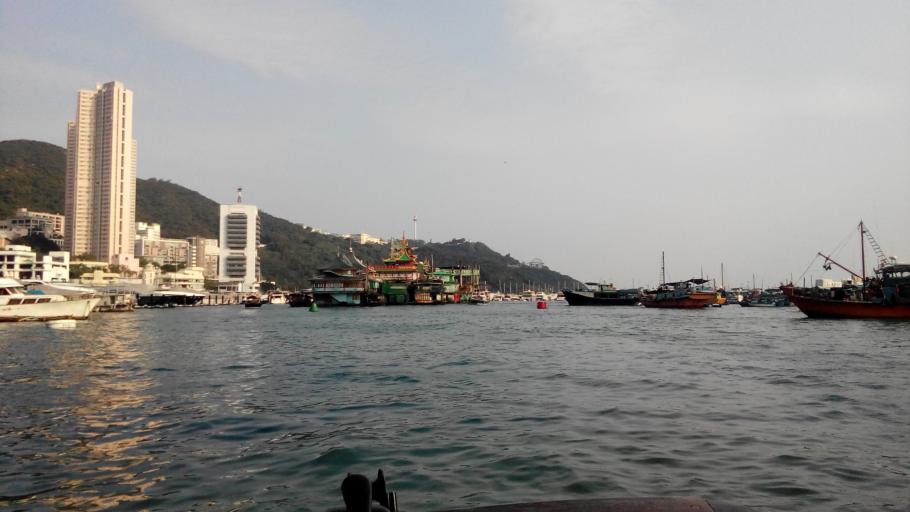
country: HK
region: Central and Western
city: Central
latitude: 22.2455
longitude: 114.1600
